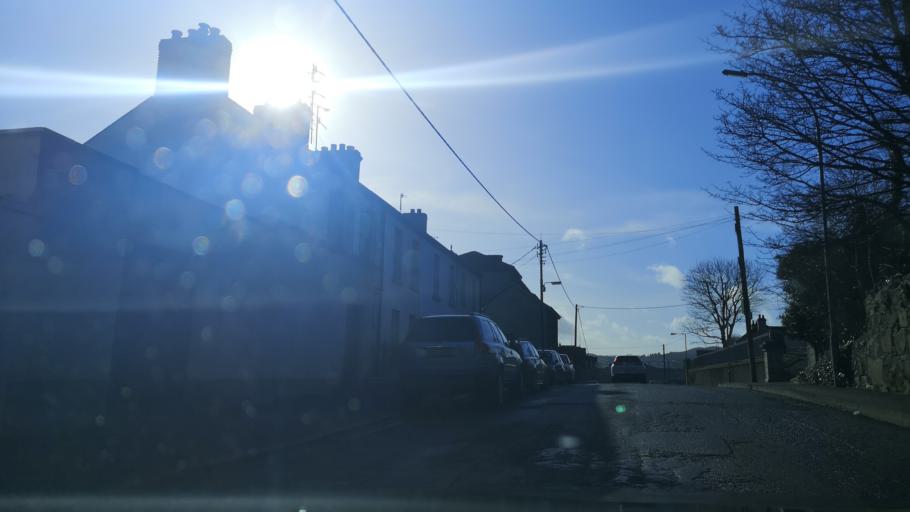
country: GB
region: Northern Ireland
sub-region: Newry and Mourne District
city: Newry
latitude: 54.1803
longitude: -6.3408
